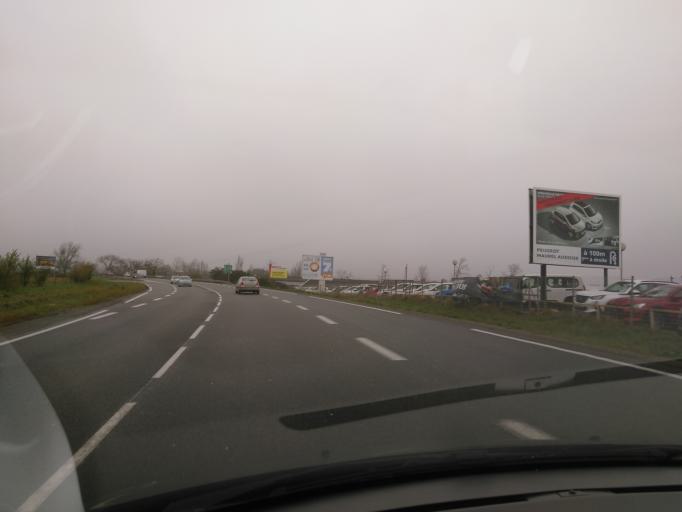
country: FR
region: Languedoc-Roussillon
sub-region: Departement de l'Aude
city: Carcassonne
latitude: 43.2130
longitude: 2.3207
